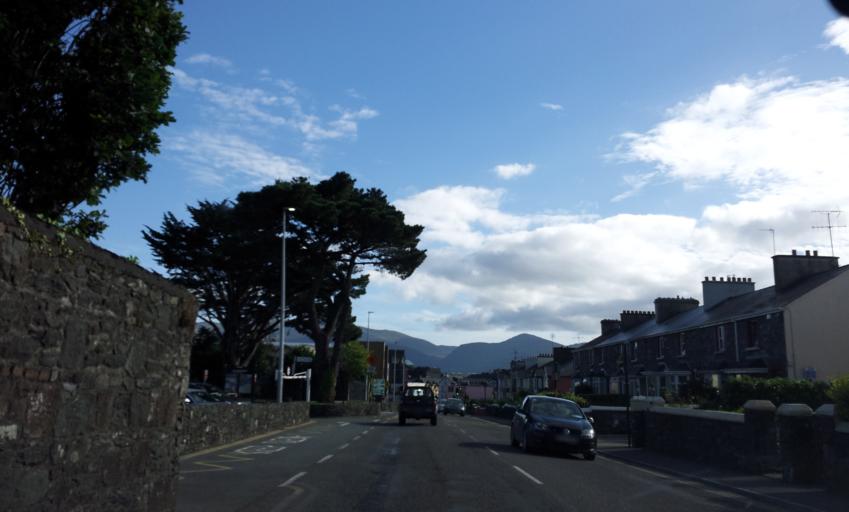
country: IE
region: Munster
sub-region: Ciarrai
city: Cill Airne
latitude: 52.0619
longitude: -9.5061
